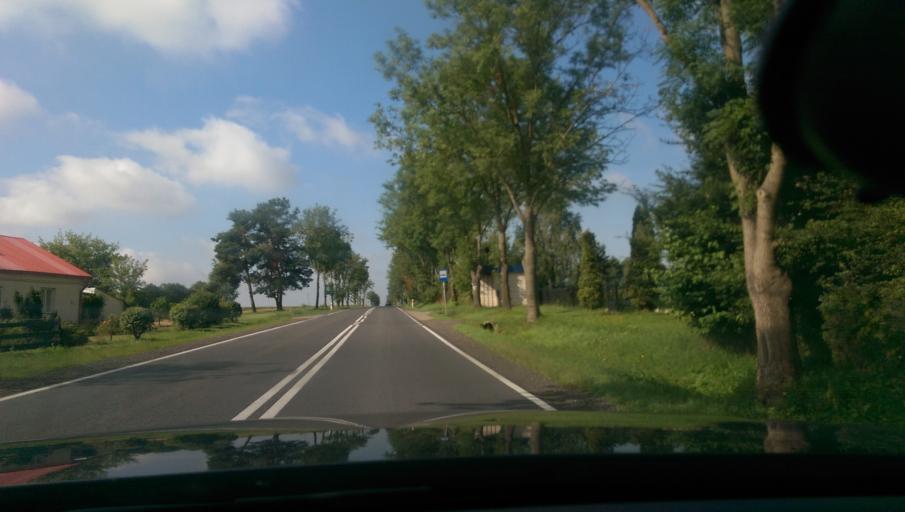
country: PL
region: Masovian Voivodeship
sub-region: Powiat plonski
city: Sochocin
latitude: 52.7064
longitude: 20.4916
